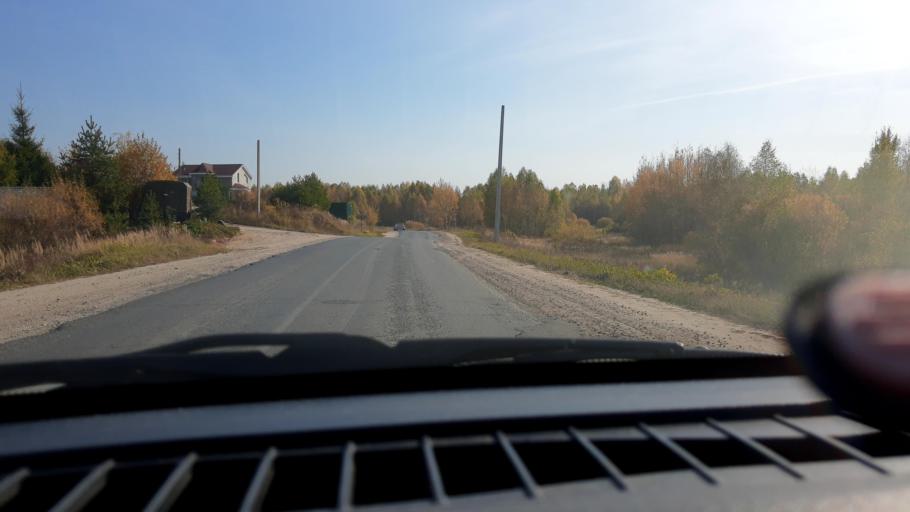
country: RU
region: Nizjnij Novgorod
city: Neklyudovo
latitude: 56.4215
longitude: 43.9310
